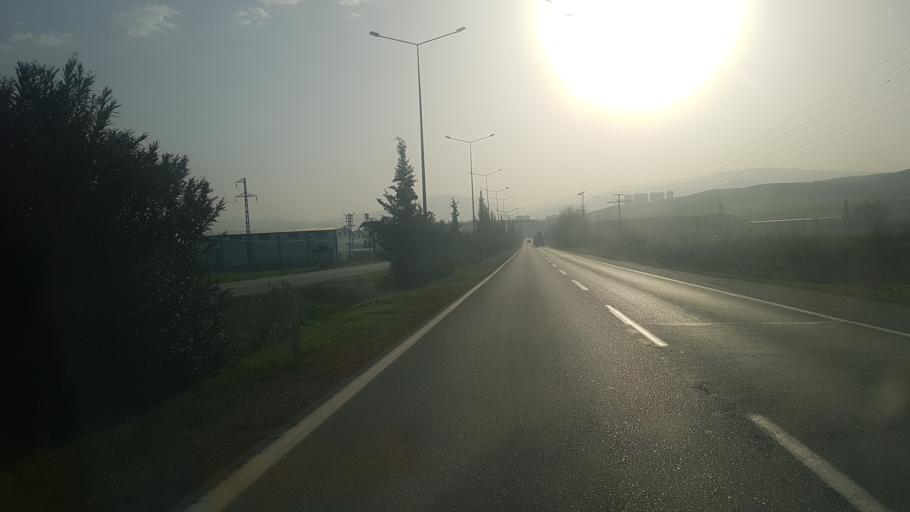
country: TR
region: Osmaniye
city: Toprakkale
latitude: 37.0538
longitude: 36.1401
